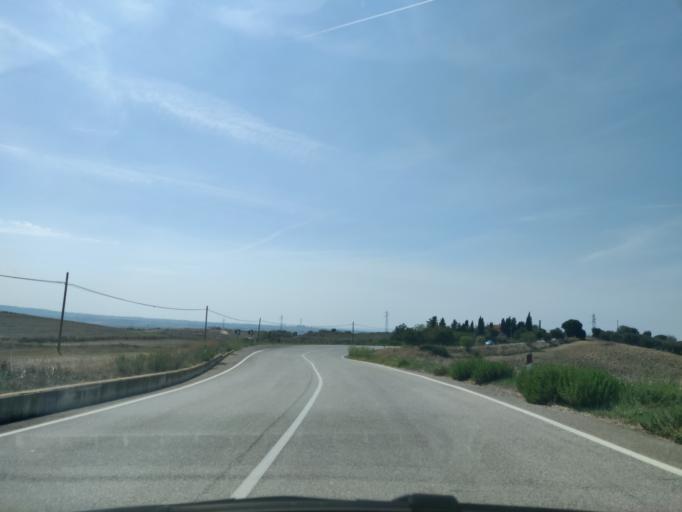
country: IT
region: Latium
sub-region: Provincia di Viterbo
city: Tarquinia
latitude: 42.2403
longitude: 11.8054
